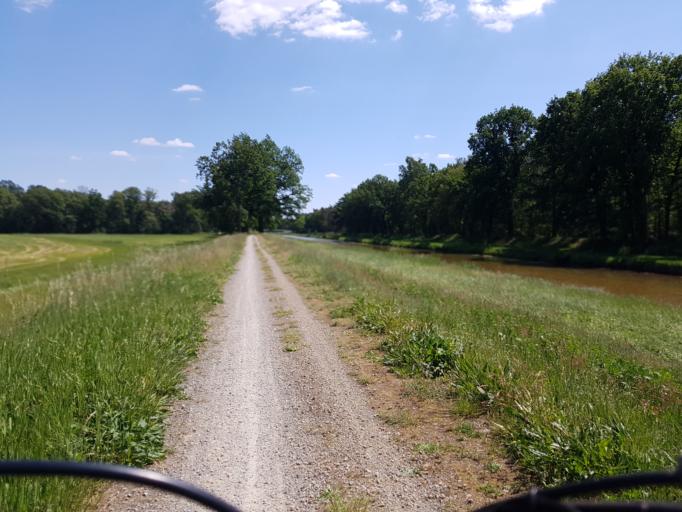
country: DE
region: Brandenburg
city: Bad Liebenwerda
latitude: 51.4904
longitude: 13.4286
